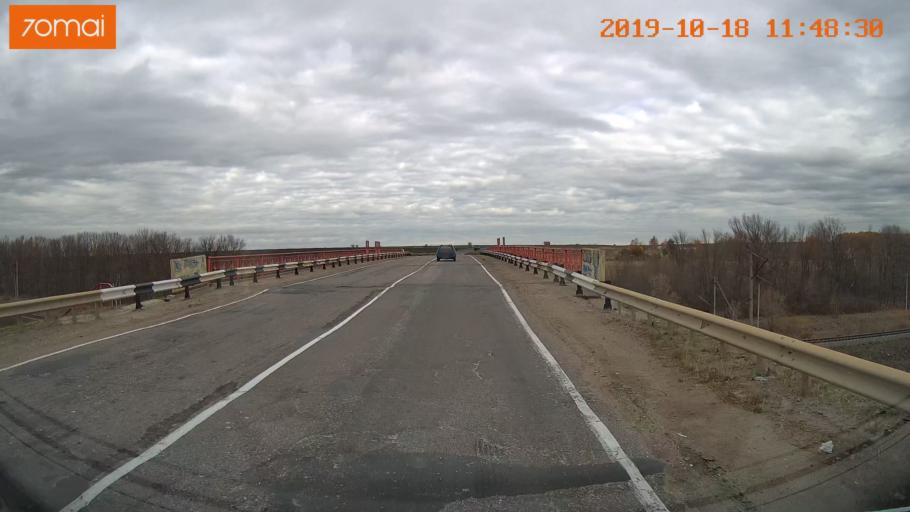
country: RU
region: Rjazan
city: Mikhaylov
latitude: 54.2400
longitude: 38.9830
